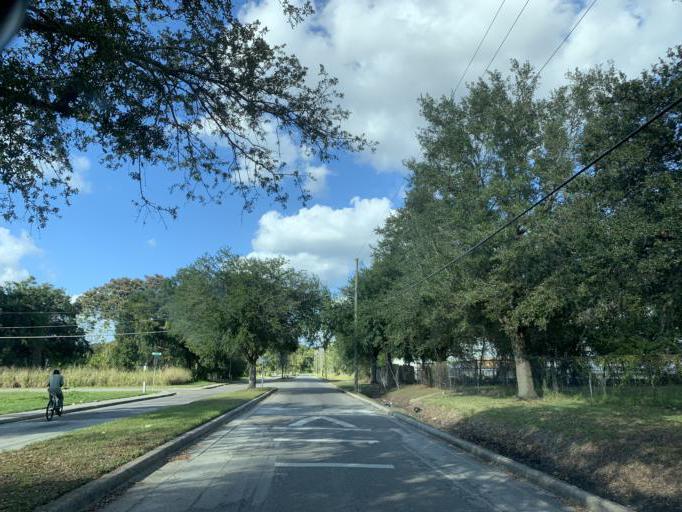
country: US
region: Florida
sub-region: Orange County
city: Eatonville
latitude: 28.6159
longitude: -81.3942
